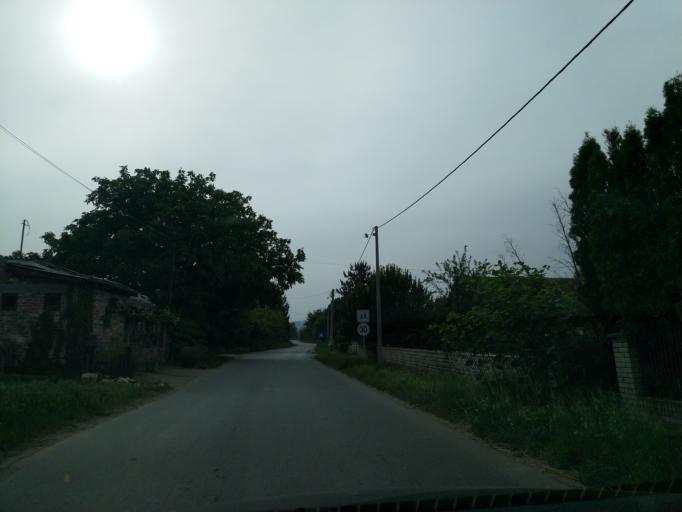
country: RS
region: Central Serbia
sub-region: Pomoravski Okrug
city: Jagodina
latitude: 43.9746
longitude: 21.2042
